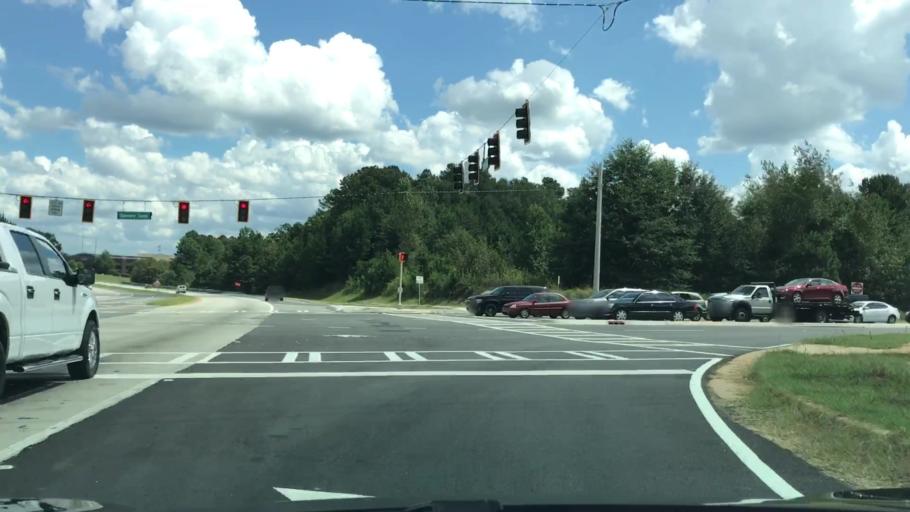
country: US
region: Georgia
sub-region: Oconee County
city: Watkinsville
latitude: 33.9111
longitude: -83.4656
